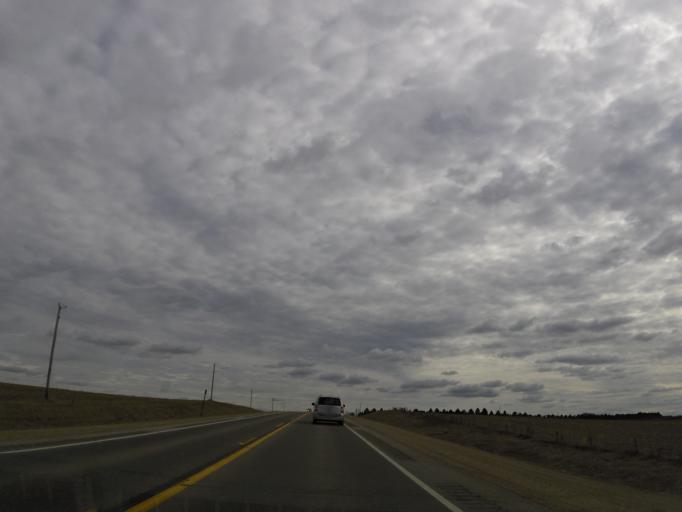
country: US
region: Iowa
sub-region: Chickasaw County
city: New Hampton
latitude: 43.1948
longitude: -92.2982
